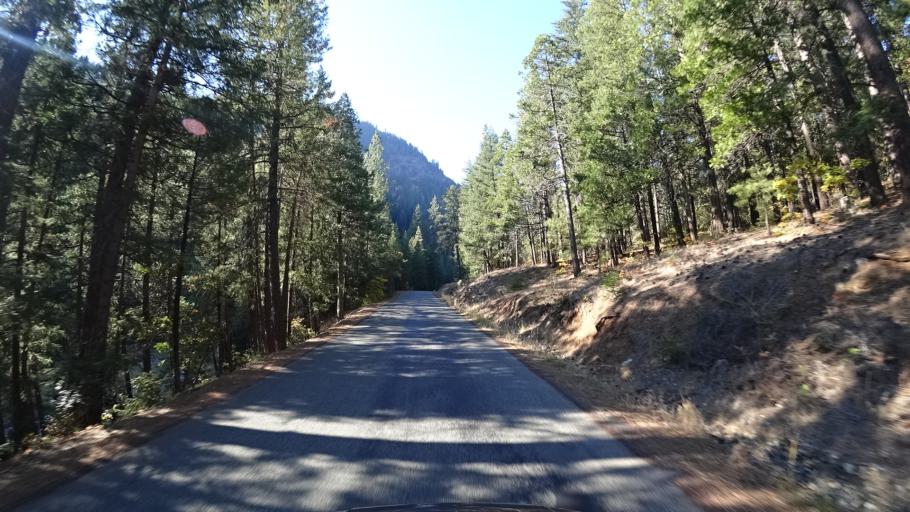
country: US
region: California
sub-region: Siskiyou County
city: Happy Camp
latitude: 41.6412
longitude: -123.0518
